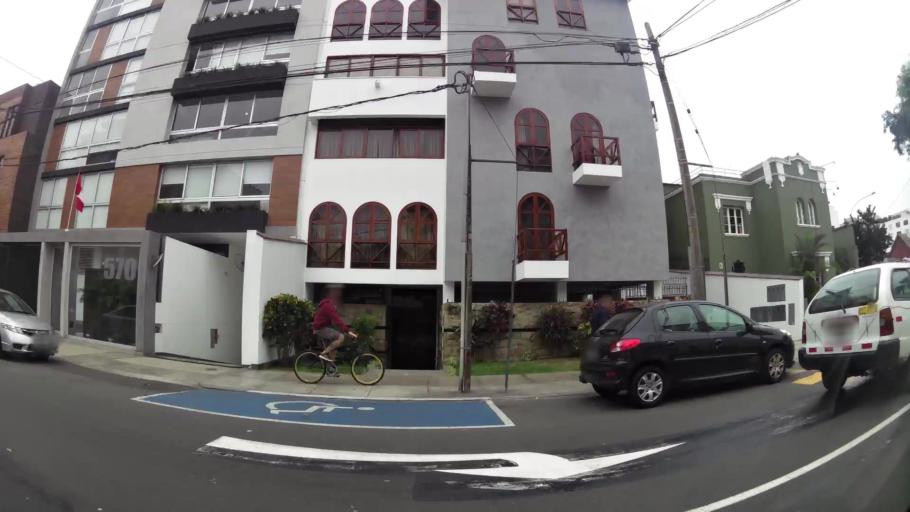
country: PE
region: Lima
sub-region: Lima
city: San Isidro
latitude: -12.1239
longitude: -77.0358
